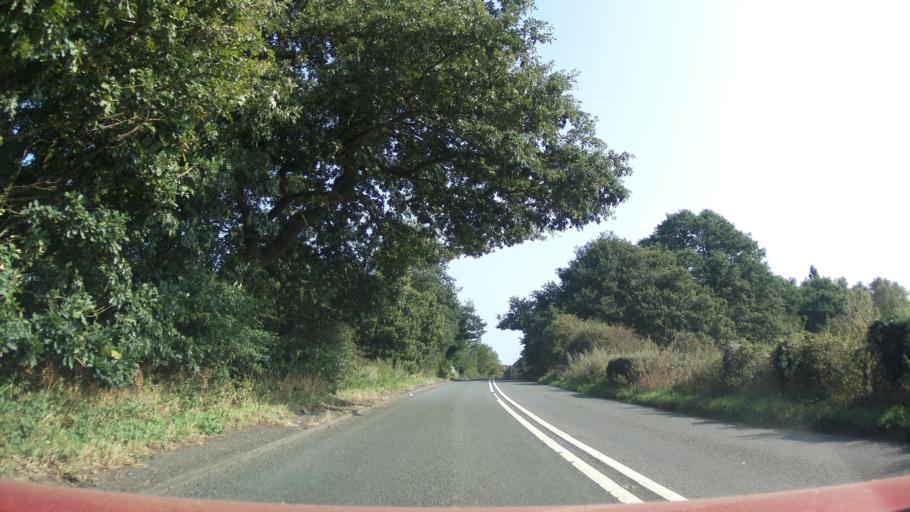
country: GB
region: England
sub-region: Staffordshire
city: Lichfield
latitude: 52.6667
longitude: -1.8700
